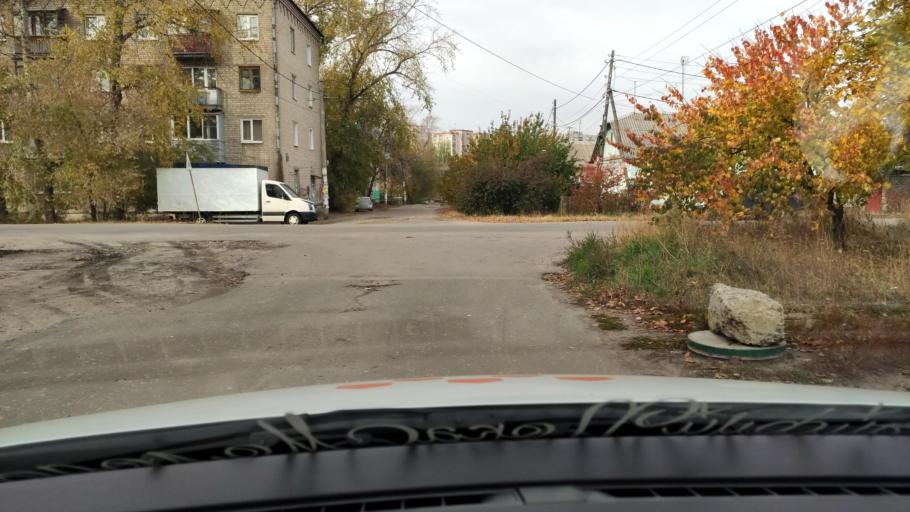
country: RU
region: Voronezj
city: Voronezh
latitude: 51.6801
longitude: 39.1364
